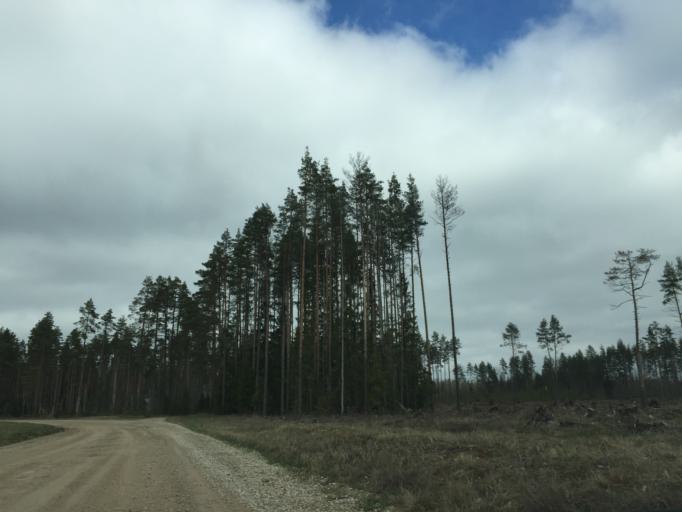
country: EE
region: Valgamaa
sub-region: Valga linn
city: Valga
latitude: 57.6484
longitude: 26.2215
